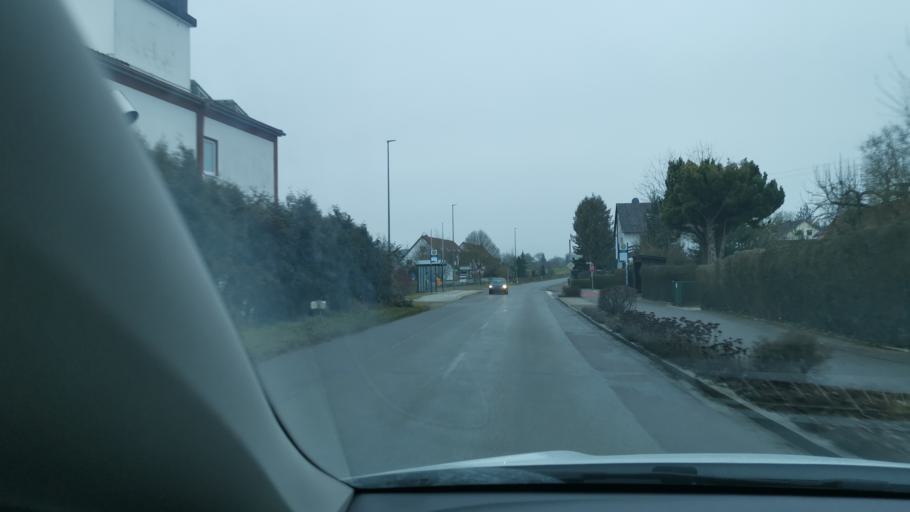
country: DE
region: Bavaria
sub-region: Swabia
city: Holzheim
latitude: 48.5891
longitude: 10.9601
